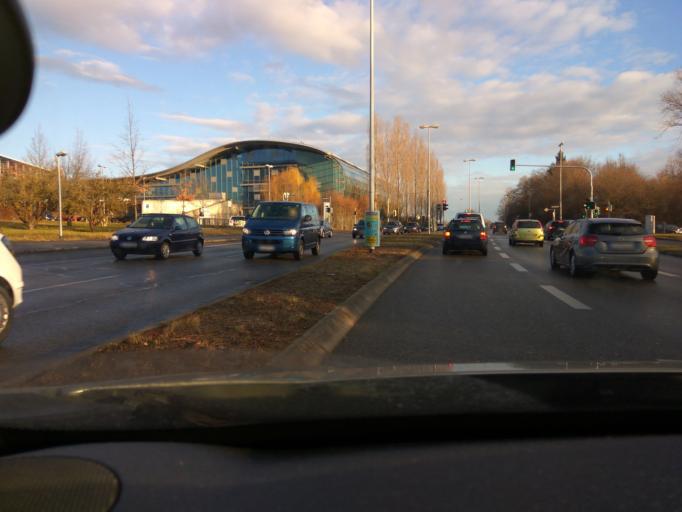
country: DE
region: Baden-Wuerttemberg
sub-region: Tuebingen Region
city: Reutlingen
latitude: 48.5163
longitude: 9.2011
